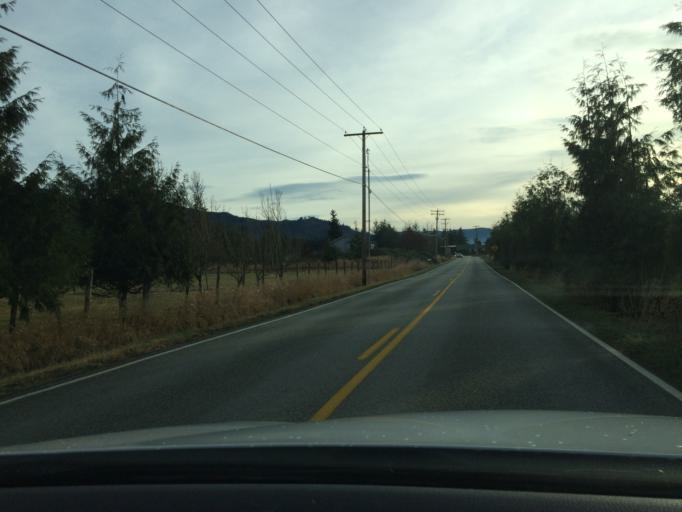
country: US
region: Washington
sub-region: Whatcom County
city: Nooksack
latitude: 48.9223
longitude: -122.2878
